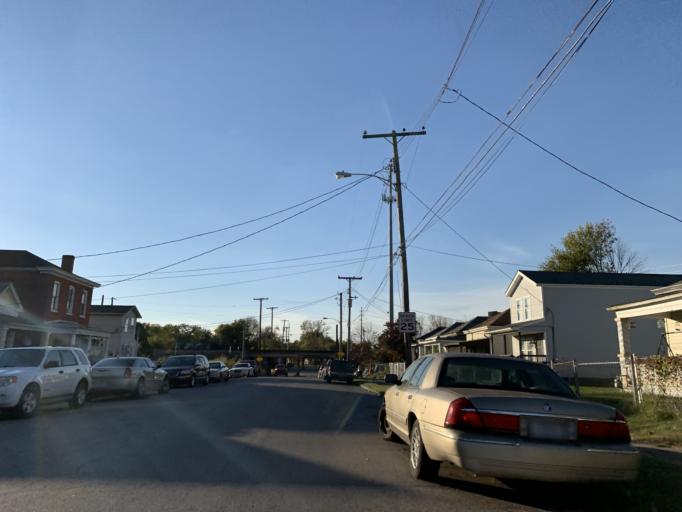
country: US
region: Indiana
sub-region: Floyd County
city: New Albany
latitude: 38.2743
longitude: -85.7945
